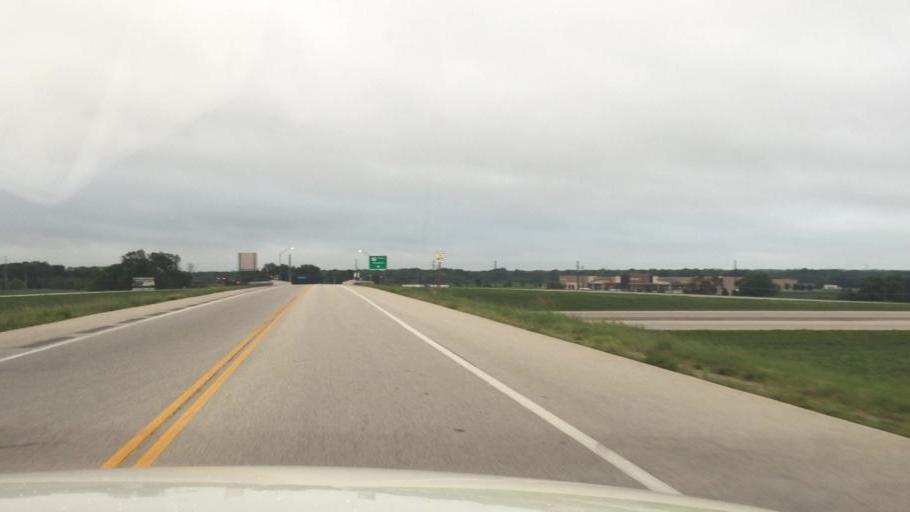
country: US
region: Kansas
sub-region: Montgomery County
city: Coffeyville
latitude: 37.0472
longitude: -95.5841
